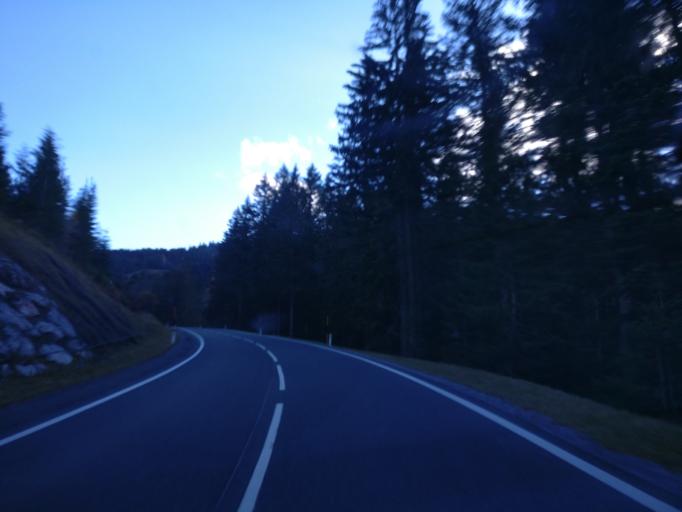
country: AT
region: Salzburg
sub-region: Politischer Bezirk Zell am See
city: Dienten am Hochkonig
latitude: 47.4017
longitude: 12.9929
